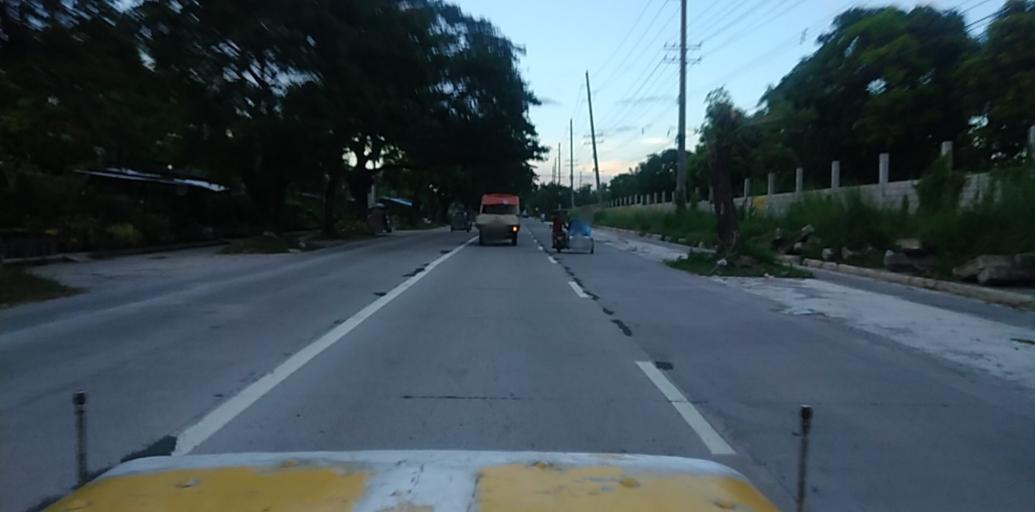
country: PH
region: Central Luzon
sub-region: Province of Pampanga
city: Calibutbut
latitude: 15.1199
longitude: 120.5892
